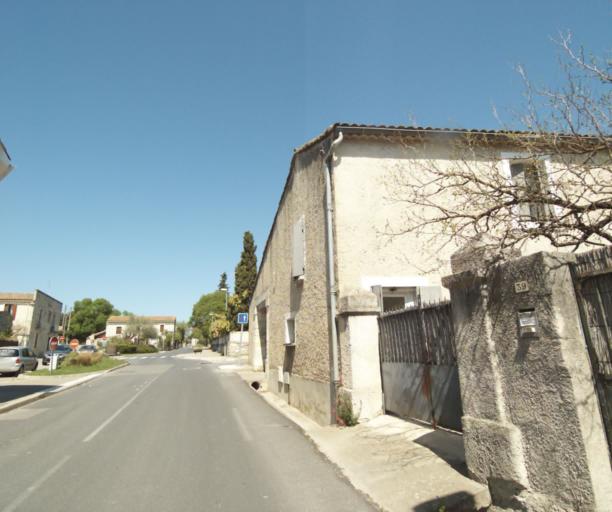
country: FR
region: Languedoc-Roussillon
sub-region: Departement de l'Herault
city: Sussargues
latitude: 43.7091
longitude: 4.0053
